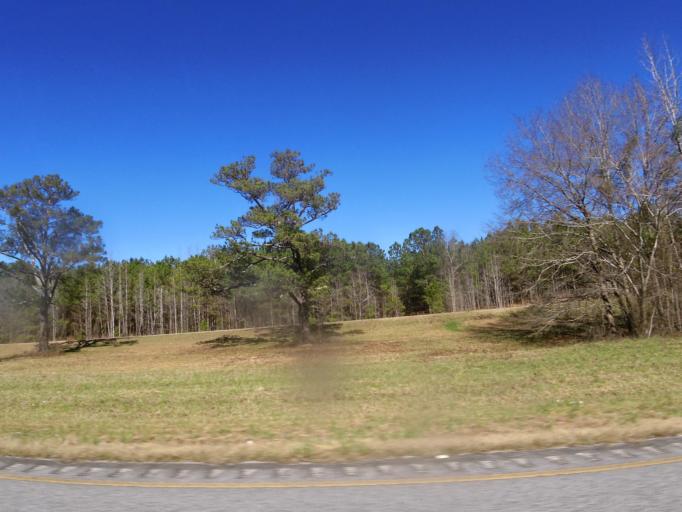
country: US
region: Alabama
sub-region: Bullock County
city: Union Springs
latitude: 32.1412
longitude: -85.6144
